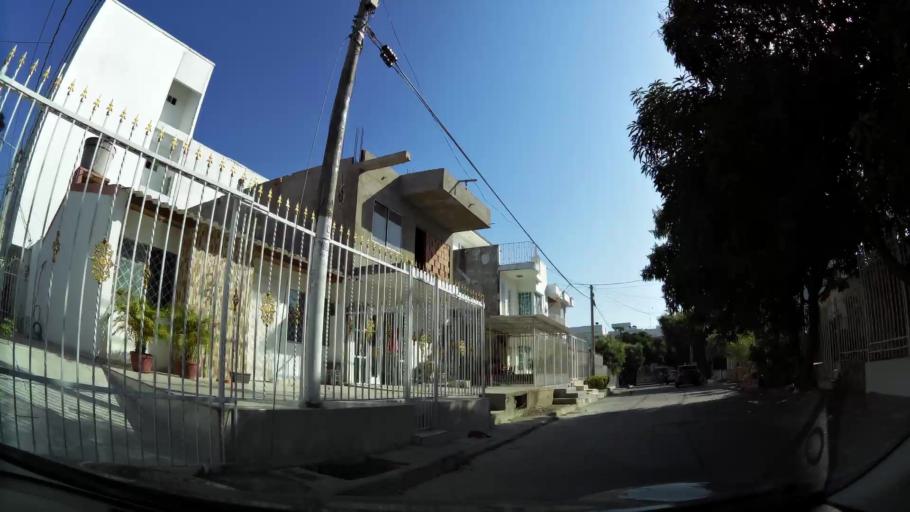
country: CO
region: Bolivar
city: Cartagena
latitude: 10.3915
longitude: -75.4988
